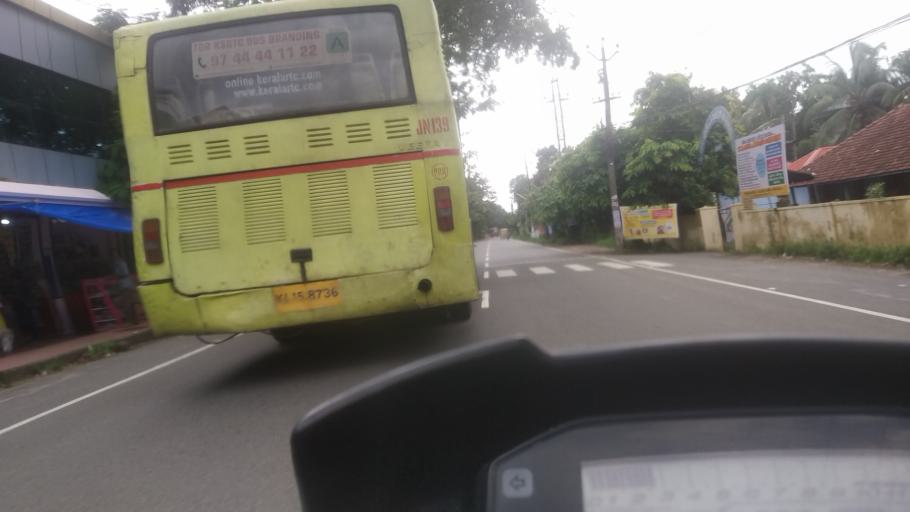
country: IN
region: Kerala
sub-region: Ernakulam
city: Elur
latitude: 10.1373
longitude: 76.2689
